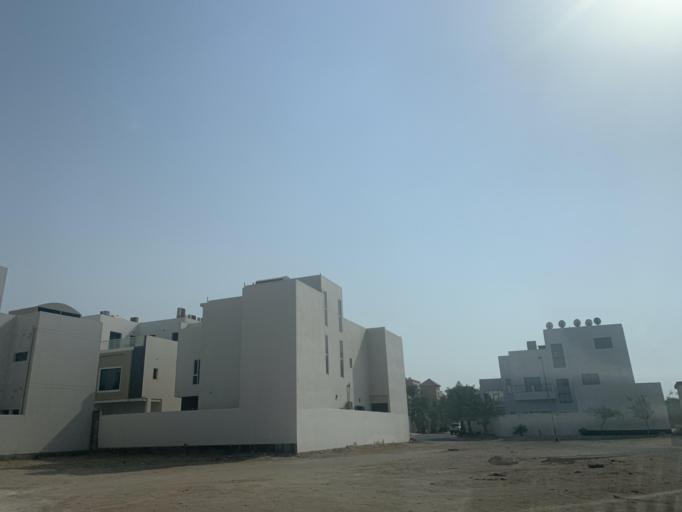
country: BH
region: Manama
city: Jidd Hafs
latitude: 26.2057
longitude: 50.4897
